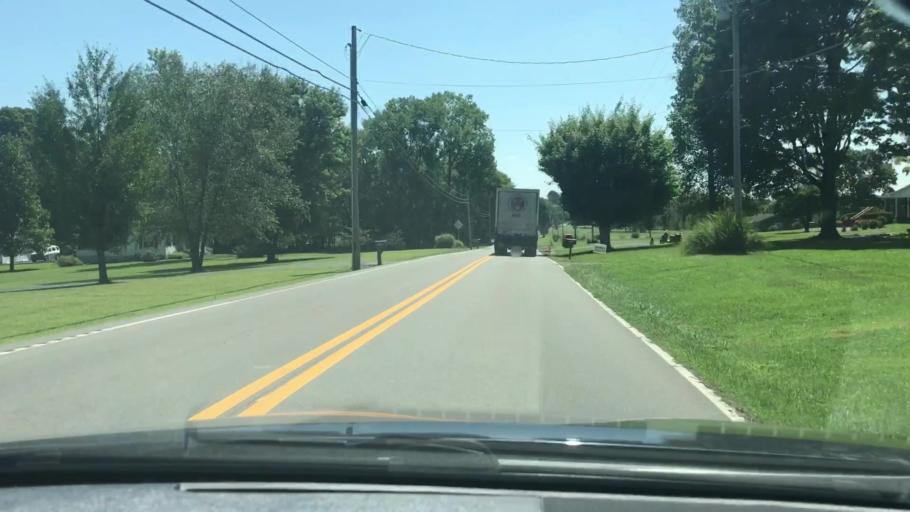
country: US
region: Tennessee
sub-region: Sumner County
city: Gallatin
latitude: 36.4182
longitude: -86.5137
